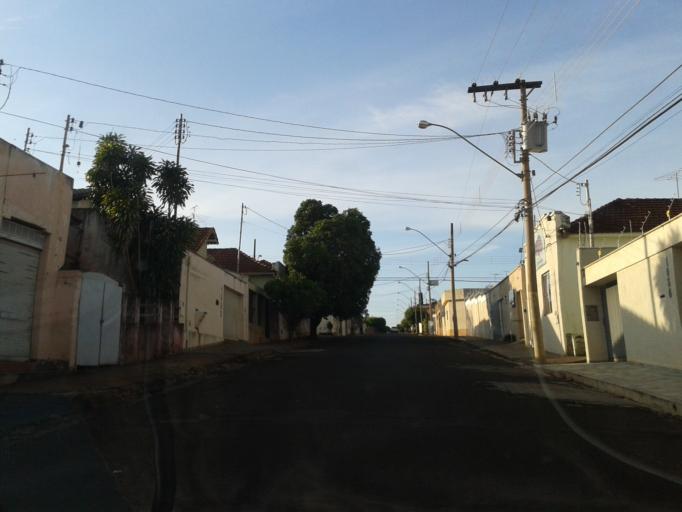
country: BR
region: Minas Gerais
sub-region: Ituiutaba
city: Ituiutaba
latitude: -18.9783
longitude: -49.4628
